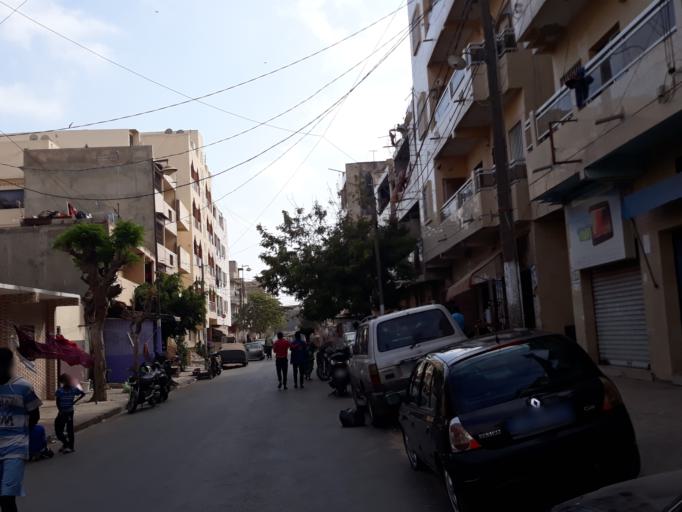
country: SN
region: Dakar
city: Dakar
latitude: 14.6898
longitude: -17.4490
